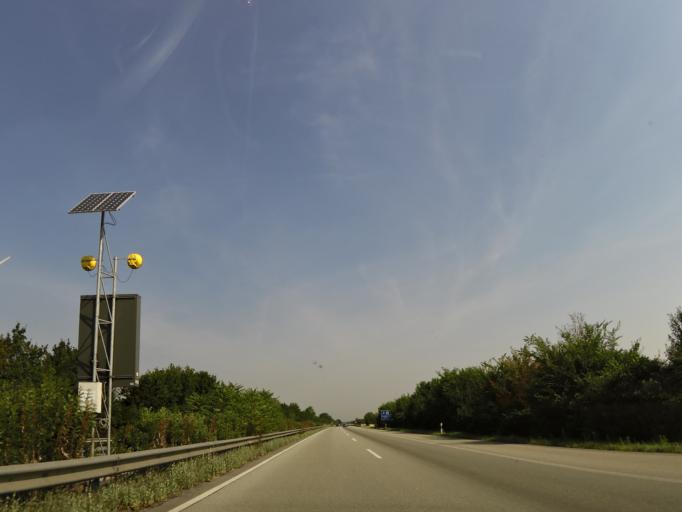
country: DE
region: Rheinland-Pfalz
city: Heuchelheim bei Frankenthal
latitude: 49.5853
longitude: 8.2923
